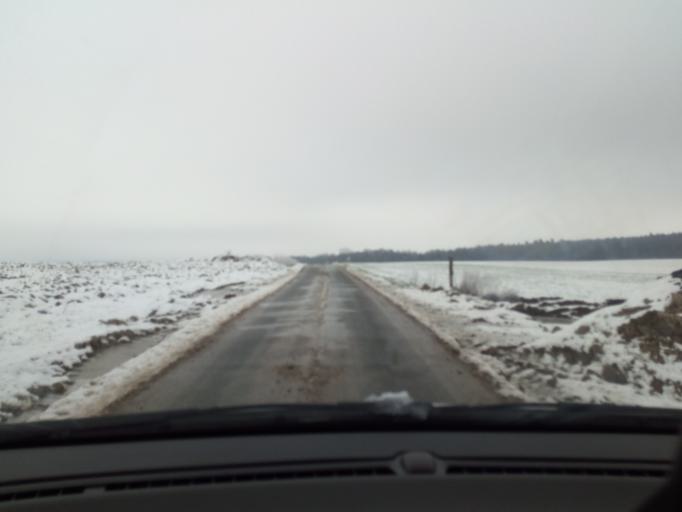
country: FR
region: Nord-Pas-de-Calais
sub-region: Departement du Nord
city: Boussois
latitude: 50.3518
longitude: 4.0243
